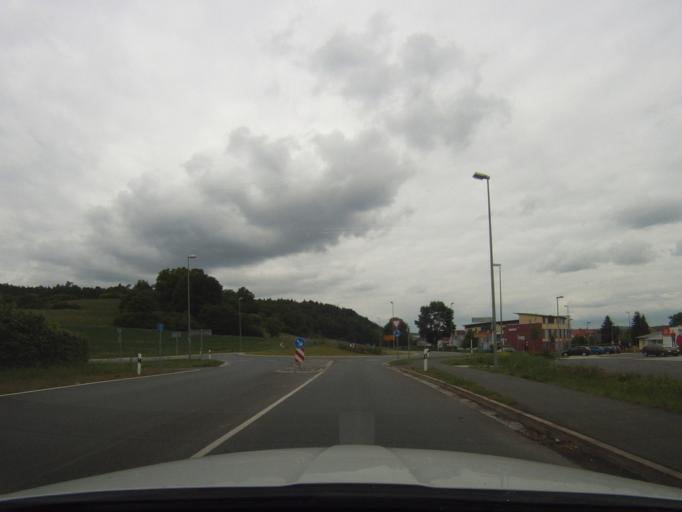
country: DE
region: Bavaria
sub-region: Upper Franconia
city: Altenkunstadt
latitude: 50.1202
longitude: 11.2322
